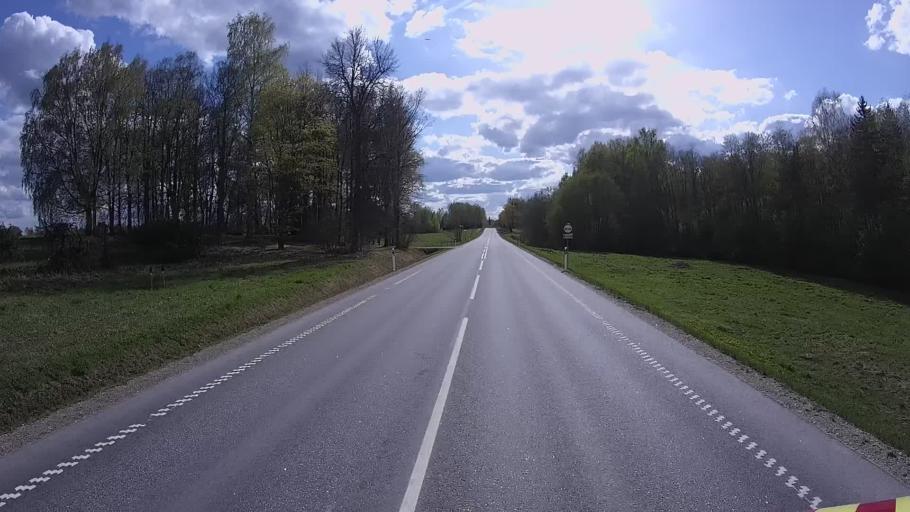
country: EE
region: Jogevamaa
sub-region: Mustvee linn
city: Mustvee
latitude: 58.8391
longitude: 26.8156
